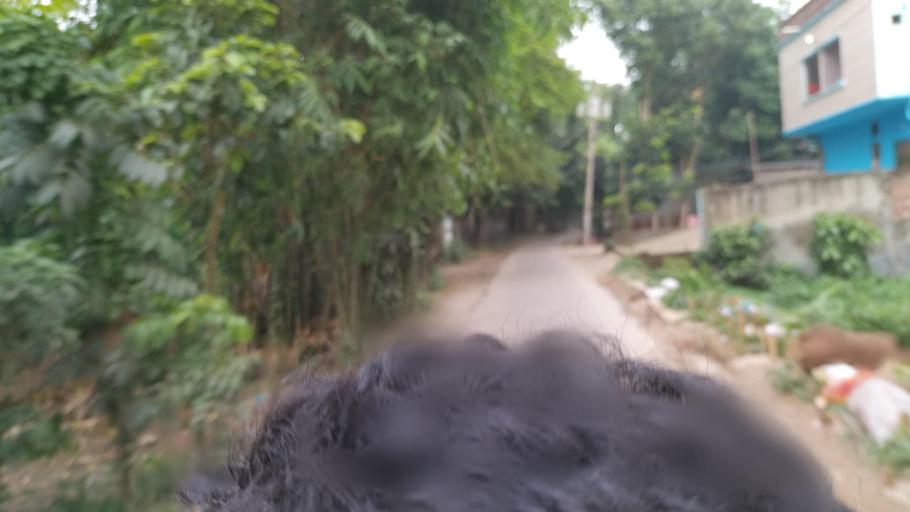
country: BD
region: Dhaka
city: Azimpur
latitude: 23.6842
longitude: 90.3105
